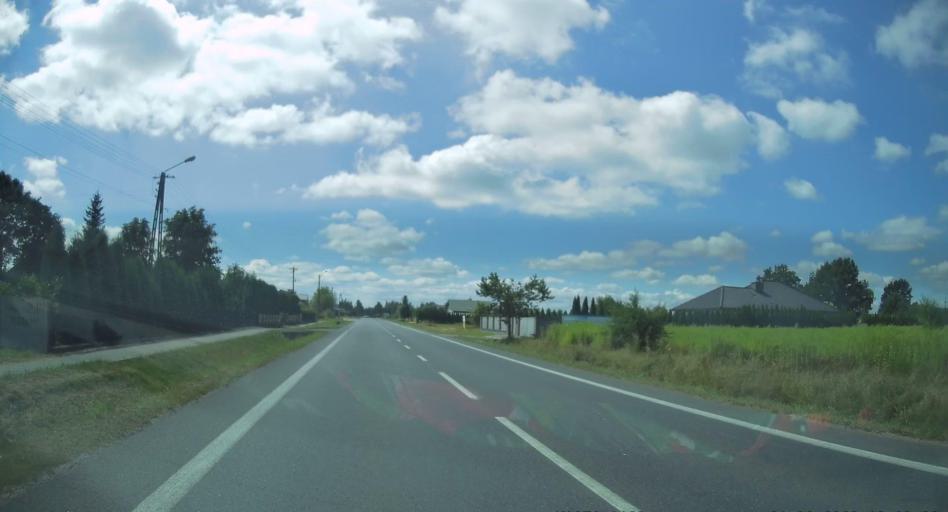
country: PL
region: Subcarpathian Voivodeship
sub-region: Powiat mielecki
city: Przeclaw
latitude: 50.1750
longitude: 21.4931
